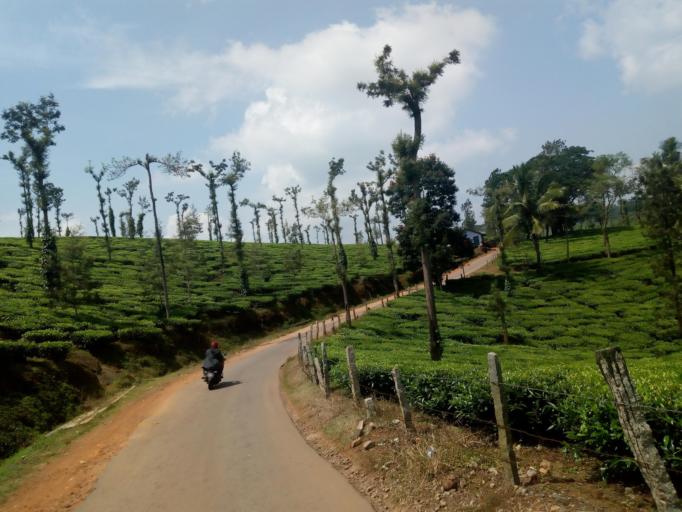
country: IN
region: Karnataka
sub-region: Kodagu
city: Ponnampet
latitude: 12.0309
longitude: 75.9429
